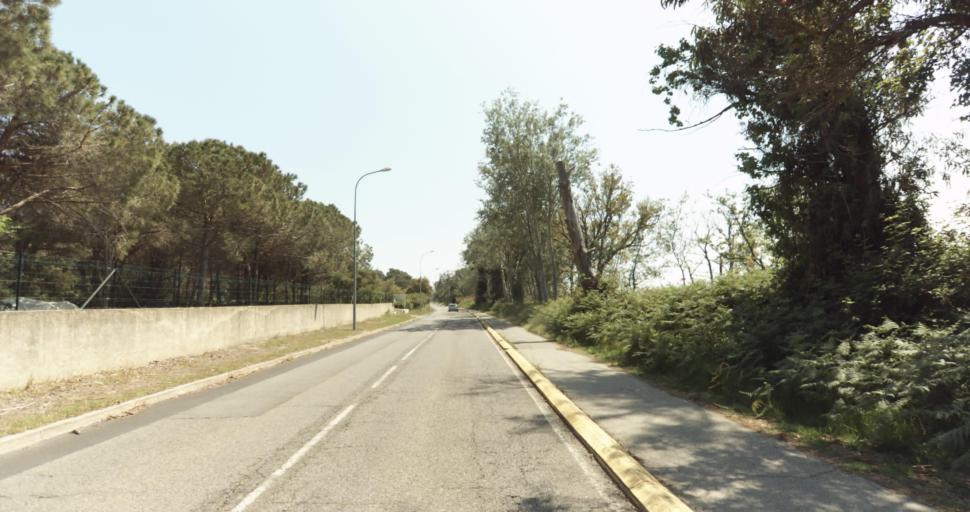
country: FR
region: Corsica
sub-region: Departement de la Haute-Corse
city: Biguglia
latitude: 42.6337
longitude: 9.4633
